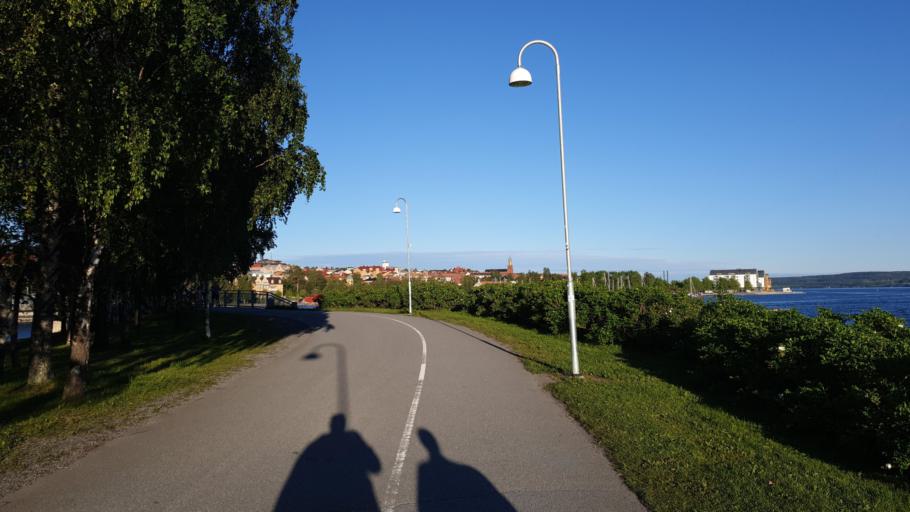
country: SE
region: Jaemtland
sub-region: OEstersunds Kommun
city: Ostersund
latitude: 63.1798
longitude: 14.6240
